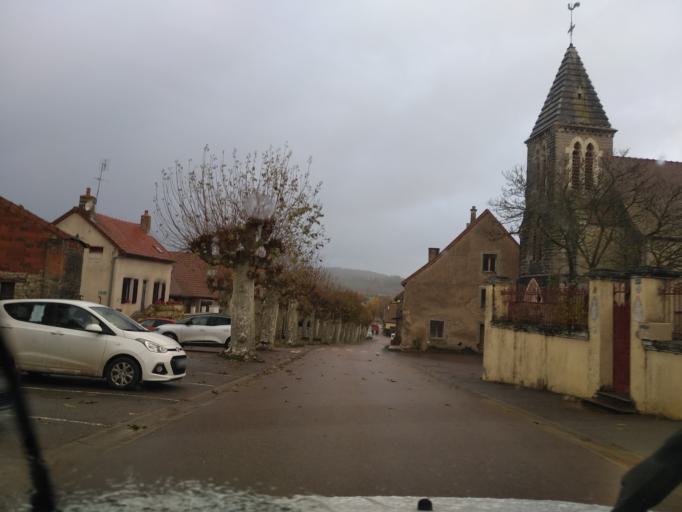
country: FR
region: Bourgogne
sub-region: Departement de Saone-et-Loire
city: Saint-Leger-sur-Dheune
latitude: 46.8776
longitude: 4.6645
